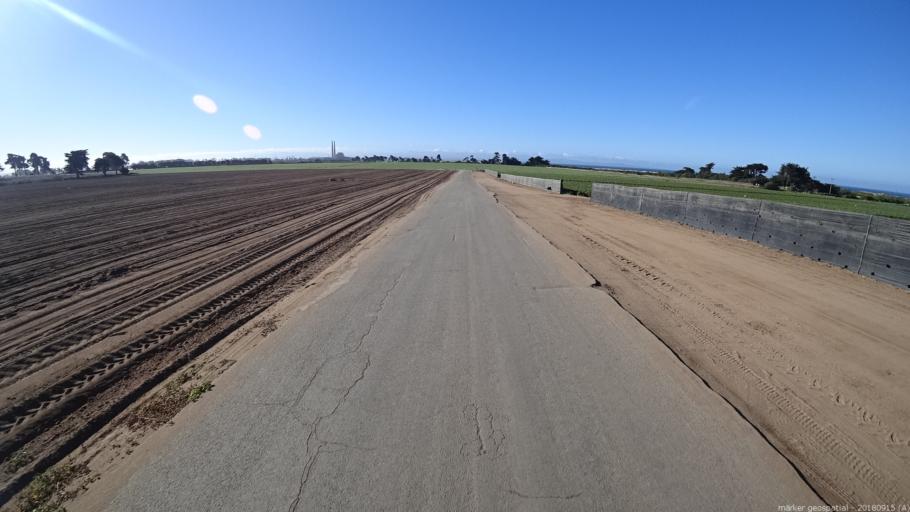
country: US
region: California
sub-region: Monterey County
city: Elkhorn
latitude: 36.8297
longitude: -121.7940
